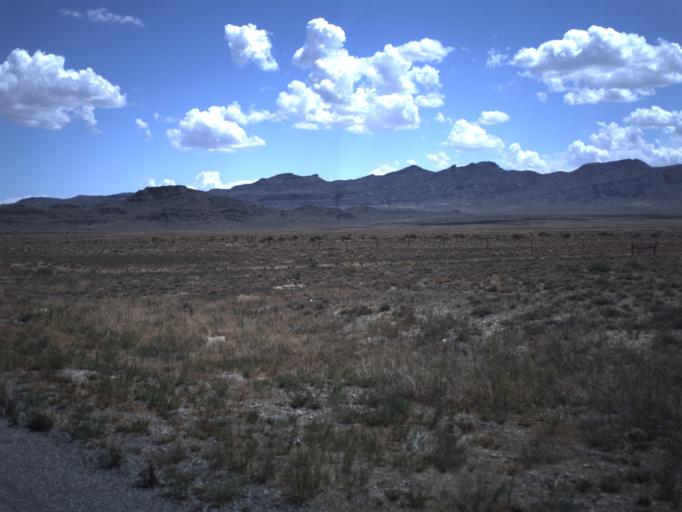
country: US
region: Utah
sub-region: Beaver County
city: Milford
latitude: 39.0564
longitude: -113.7674
